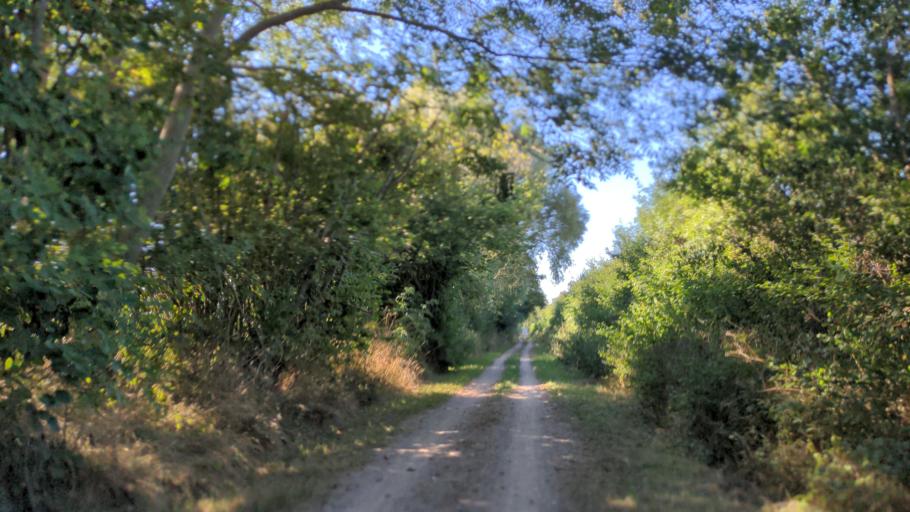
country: DE
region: Mecklenburg-Vorpommern
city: Ostseebad Boltenhagen
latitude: 53.9641
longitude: 11.2355
